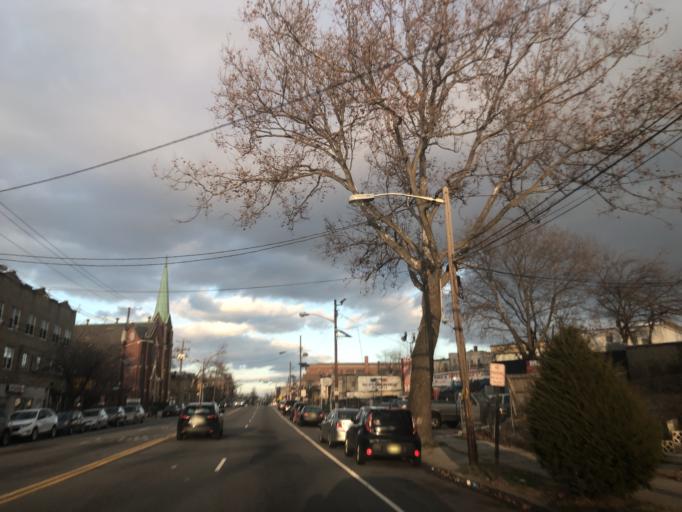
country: US
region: New Jersey
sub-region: Hudson County
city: Jersey City
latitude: 40.7008
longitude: -74.0937
